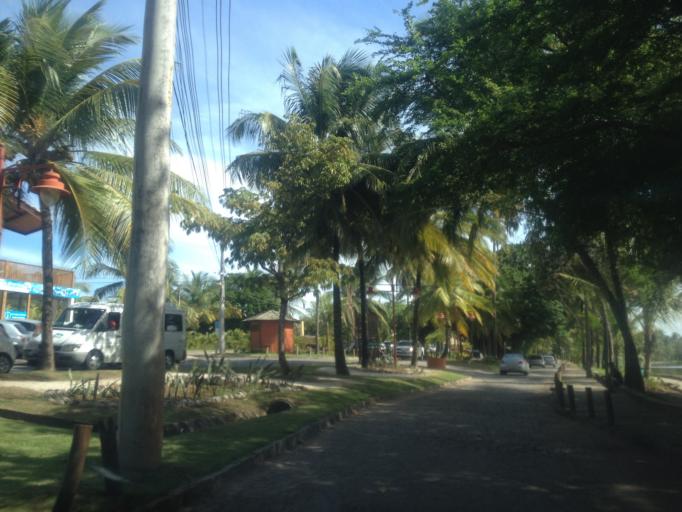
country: BR
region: Bahia
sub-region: Mata De Sao Joao
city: Mata de Sao Joao
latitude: -12.5771
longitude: -38.0091
